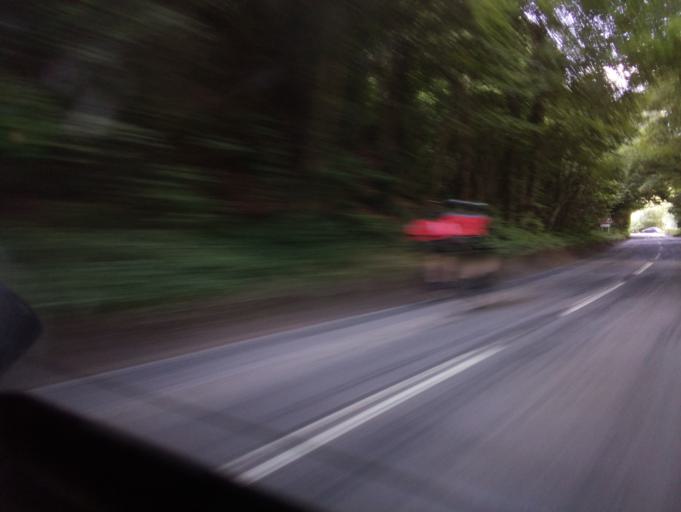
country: GB
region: England
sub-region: Herefordshire
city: Walford
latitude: 51.8705
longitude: -2.6082
